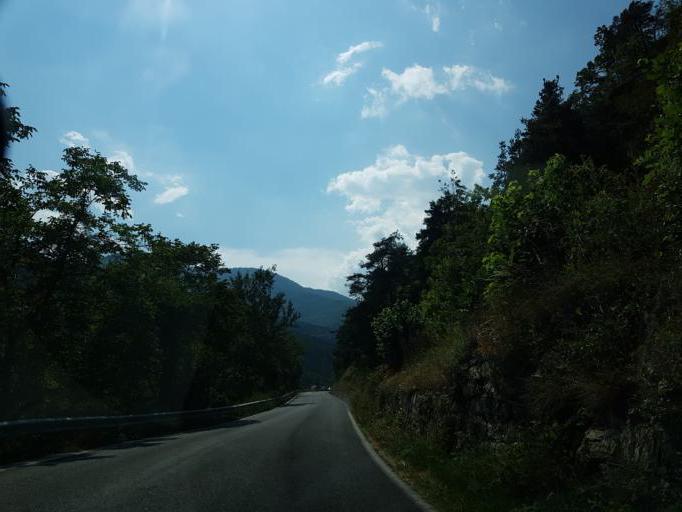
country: IT
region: Piedmont
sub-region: Provincia di Cuneo
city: San Damiano Macra
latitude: 44.4902
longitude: 7.2292
